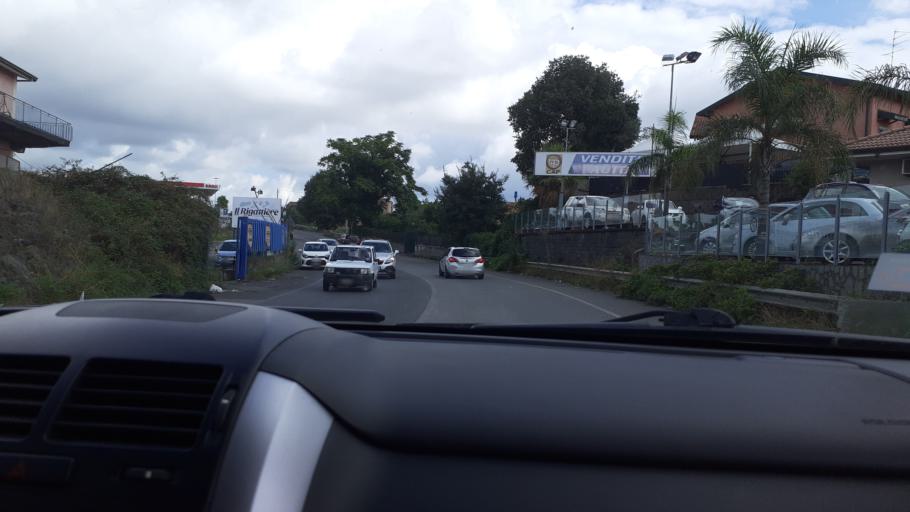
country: IT
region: Sicily
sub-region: Catania
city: San Giovanni la Punta
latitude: 37.5735
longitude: 15.1023
